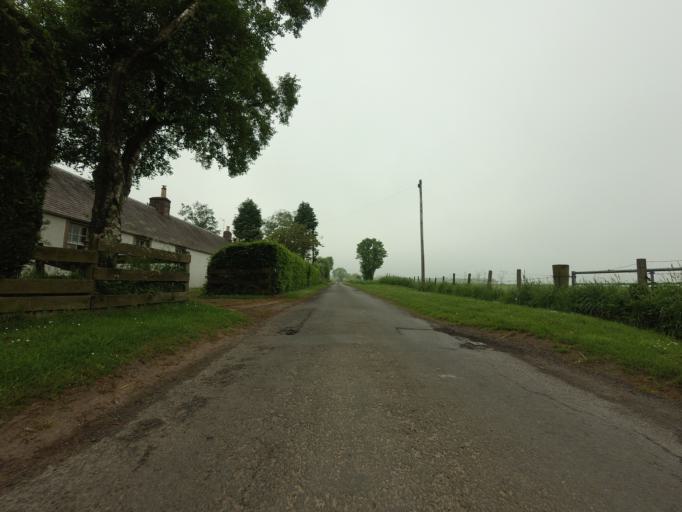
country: GB
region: Scotland
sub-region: Perth and Kinross
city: Abernethy
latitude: 56.2526
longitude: -3.3287
